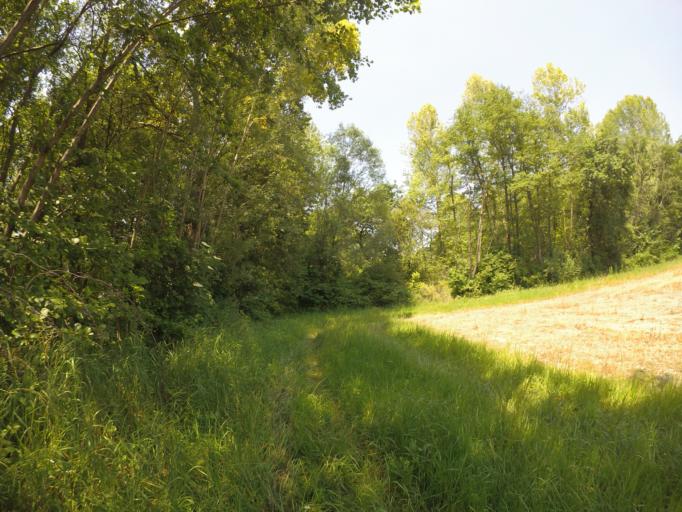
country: IT
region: Friuli Venezia Giulia
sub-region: Provincia di Udine
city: Rivignano
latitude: 45.9117
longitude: 13.0333
